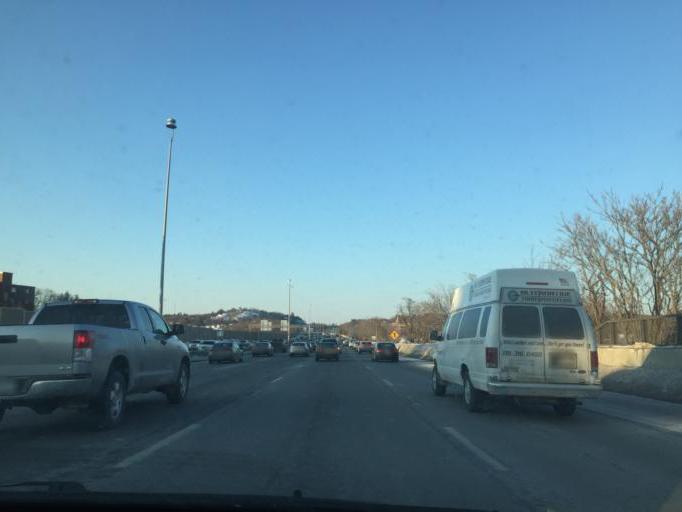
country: US
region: Massachusetts
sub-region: Middlesex County
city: Medford
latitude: 42.4200
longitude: -71.1038
